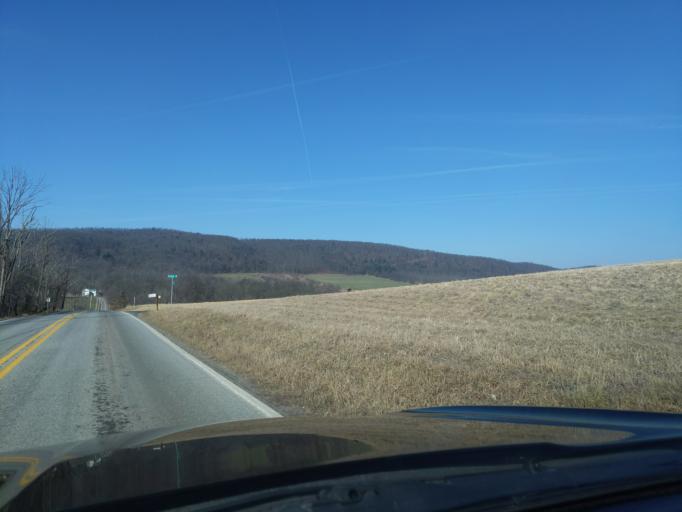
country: US
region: Pennsylvania
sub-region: Blair County
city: Tipton
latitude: 40.6148
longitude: -78.2581
